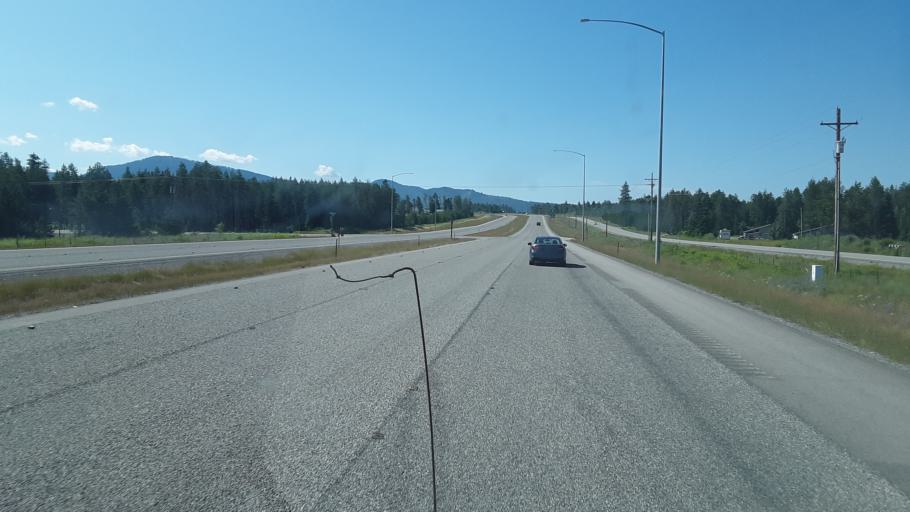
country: US
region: Idaho
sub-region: Kootenai County
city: Spirit Lake
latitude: 47.9638
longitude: -116.6991
